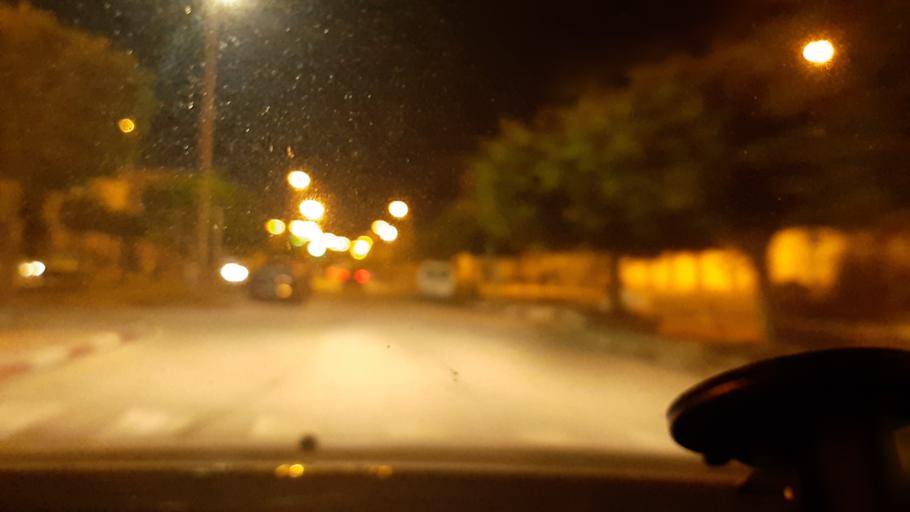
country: TN
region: Safaqis
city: Sfax
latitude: 34.7343
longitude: 10.7623
